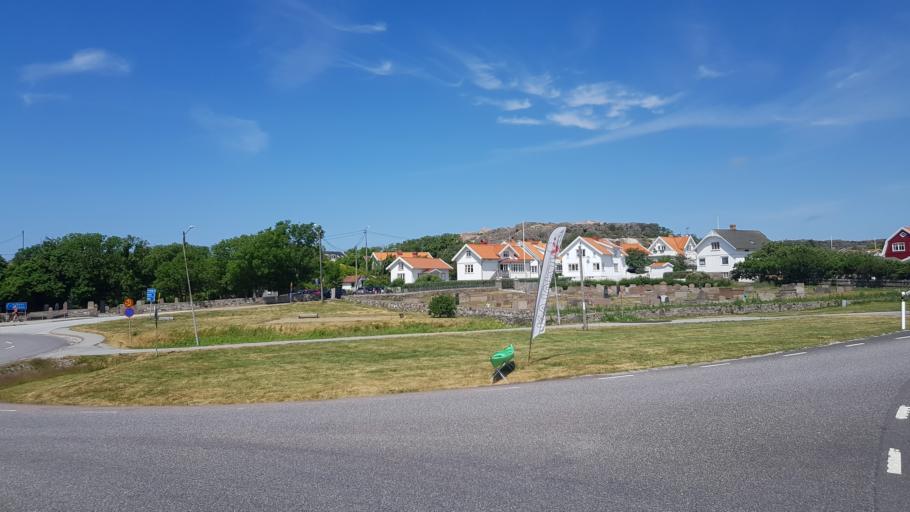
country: SE
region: Vaestra Goetaland
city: Ronnang
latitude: 57.9496
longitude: 11.5685
